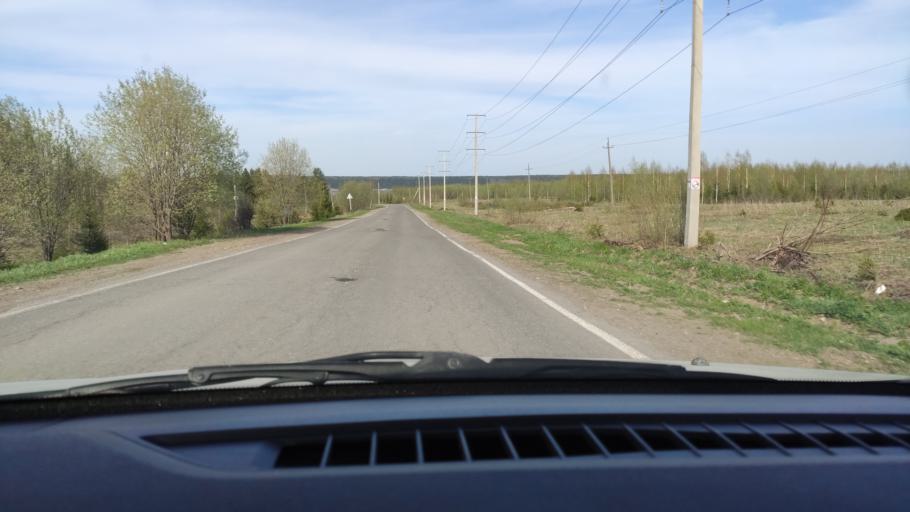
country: RU
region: Perm
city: Sylva
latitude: 57.9234
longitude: 56.6789
